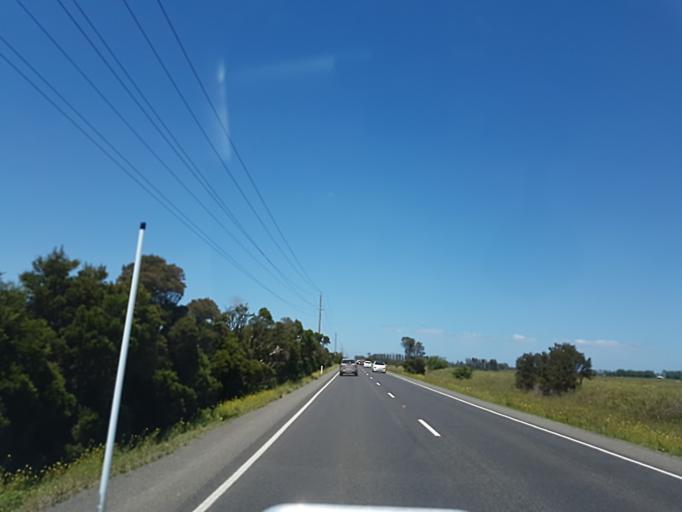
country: AU
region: Victoria
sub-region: Cardinia
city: Pakenham South
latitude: -38.1418
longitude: 145.4882
